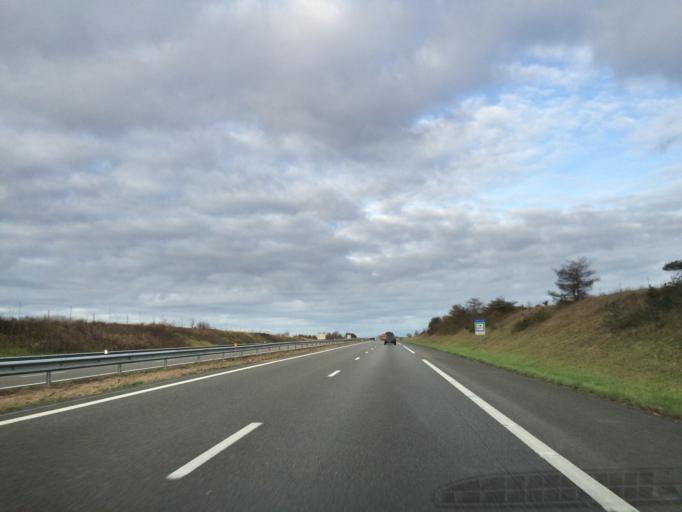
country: FR
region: Poitou-Charentes
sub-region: Departement de la Charente-Maritime
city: Saint-Jean-d'Angely
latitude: 45.9806
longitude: -0.5457
